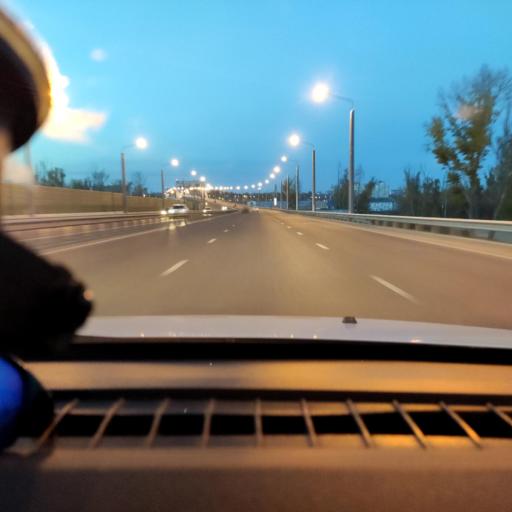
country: RU
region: Samara
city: Samara
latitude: 53.1682
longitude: 50.0856
